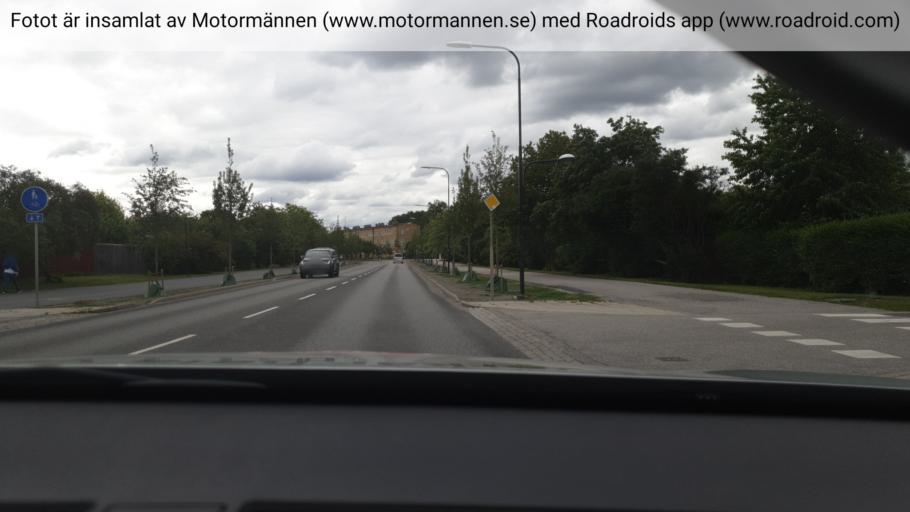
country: SE
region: Stockholm
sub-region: Stockholms Kommun
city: Arsta
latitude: 59.2858
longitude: 18.0664
